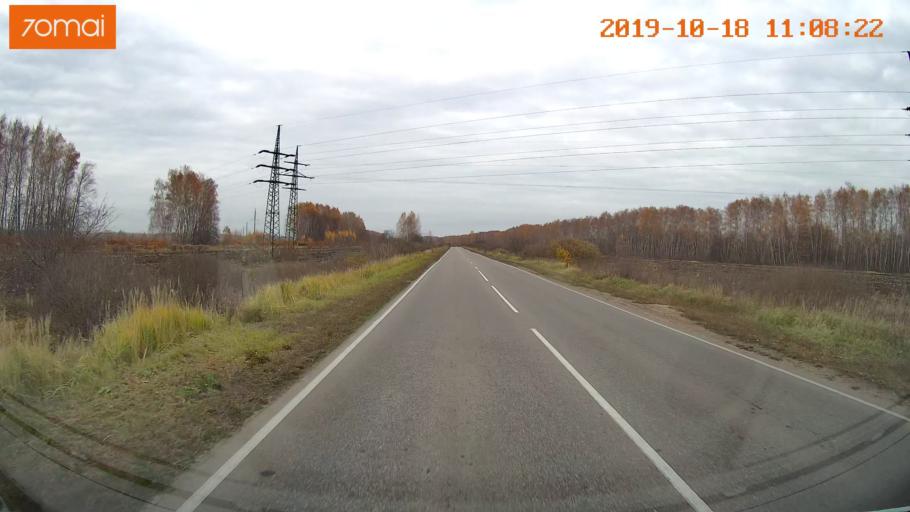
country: RU
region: Tula
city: Kimovsk
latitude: 53.9370
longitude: 38.5375
